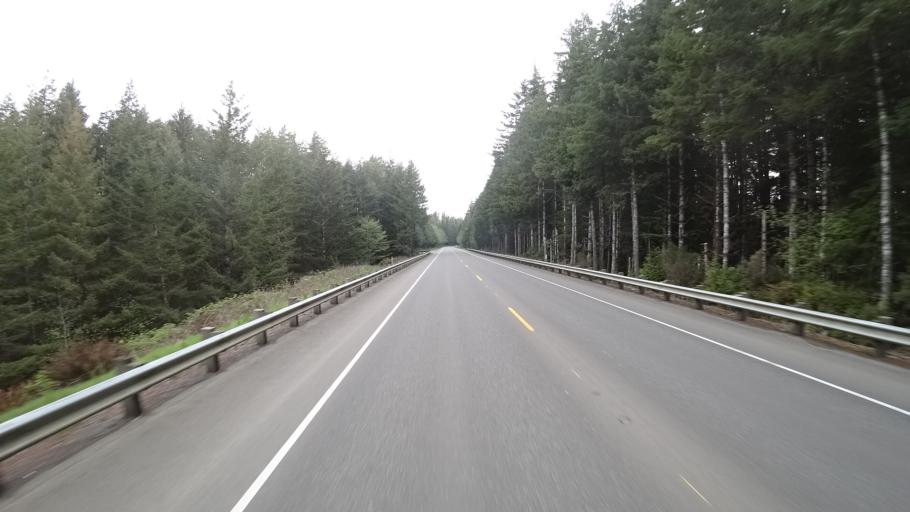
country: US
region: Oregon
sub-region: Coos County
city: Barview
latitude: 43.2498
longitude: -124.2866
